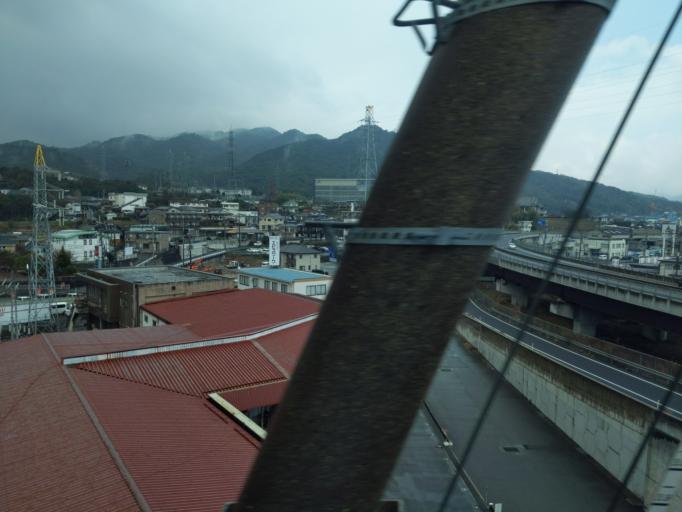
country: JP
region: Yamaguchi
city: Ogori-shimogo
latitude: 34.0898
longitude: 131.3915
